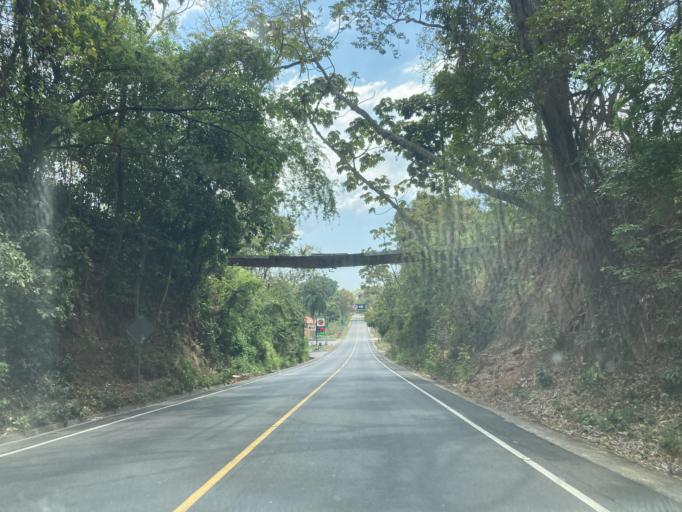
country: GT
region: Santa Rosa
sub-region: Municipio de Taxisco
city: Taxisco
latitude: 14.0653
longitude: -90.4701
